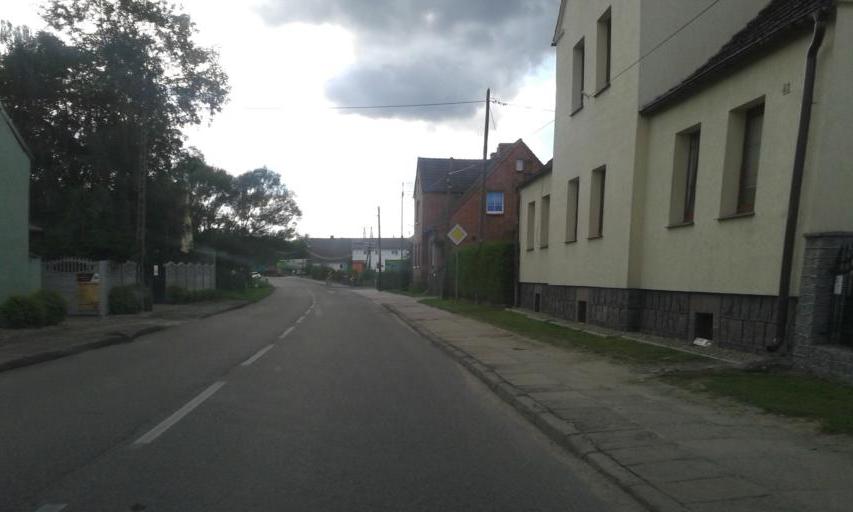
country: PL
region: West Pomeranian Voivodeship
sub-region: Powiat szczecinecki
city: Barwice
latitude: 53.7556
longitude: 16.3044
